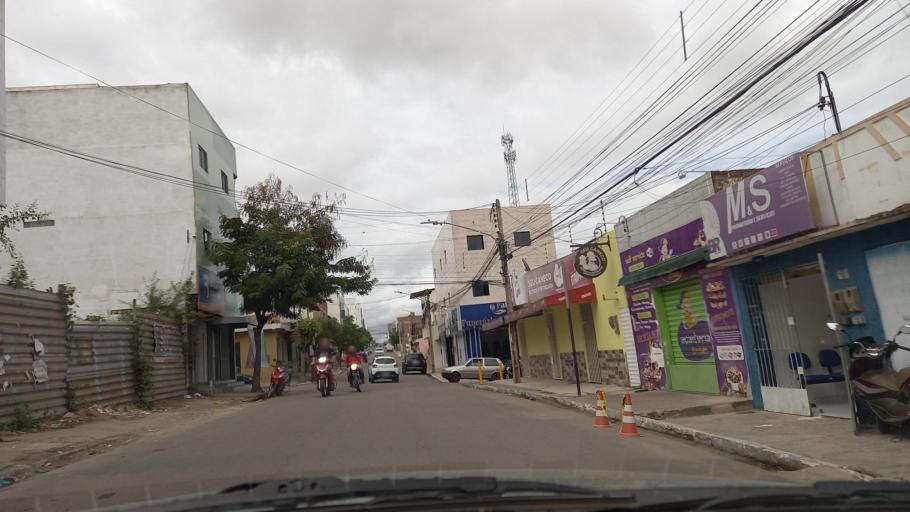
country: BR
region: Pernambuco
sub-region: Caruaru
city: Caruaru
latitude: -8.2741
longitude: -35.9599
